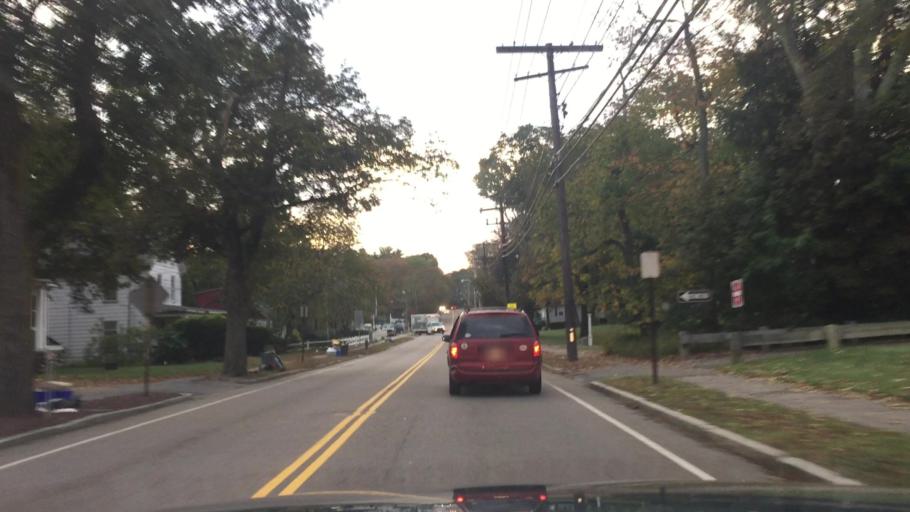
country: US
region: Massachusetts
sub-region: Norfolk County
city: Walpole
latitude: 42.1472
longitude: -71.2449
